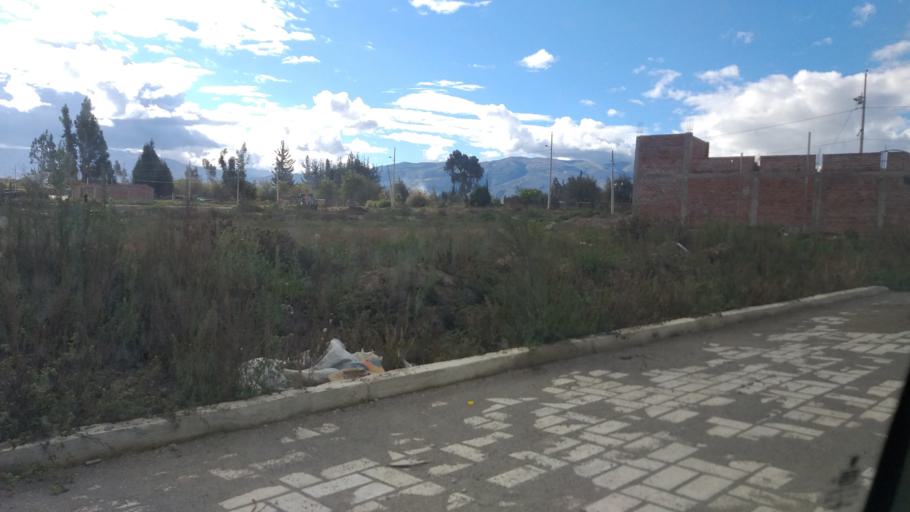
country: EC
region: Chimborazo
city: Riobamba
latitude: -1.6875
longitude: -78.6230
